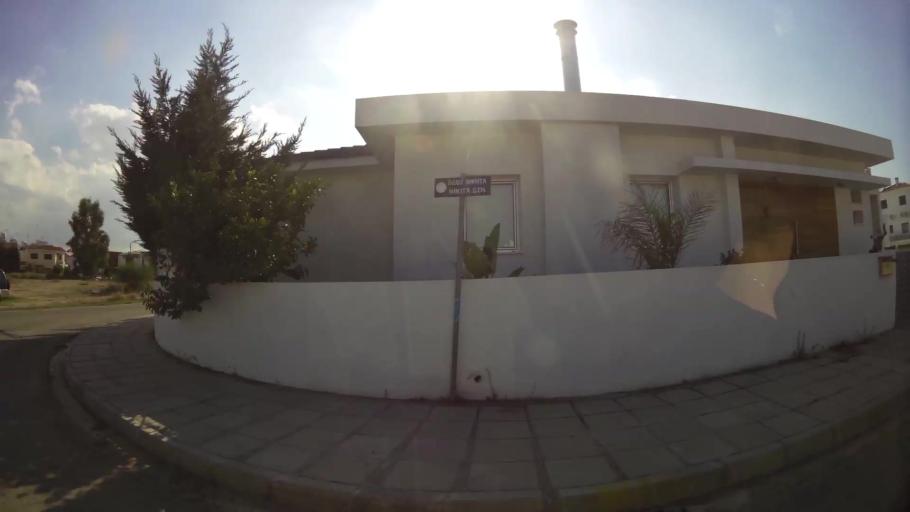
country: CY
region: Lefkosia
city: Nicosia
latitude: 35.1550
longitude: 33.3013
